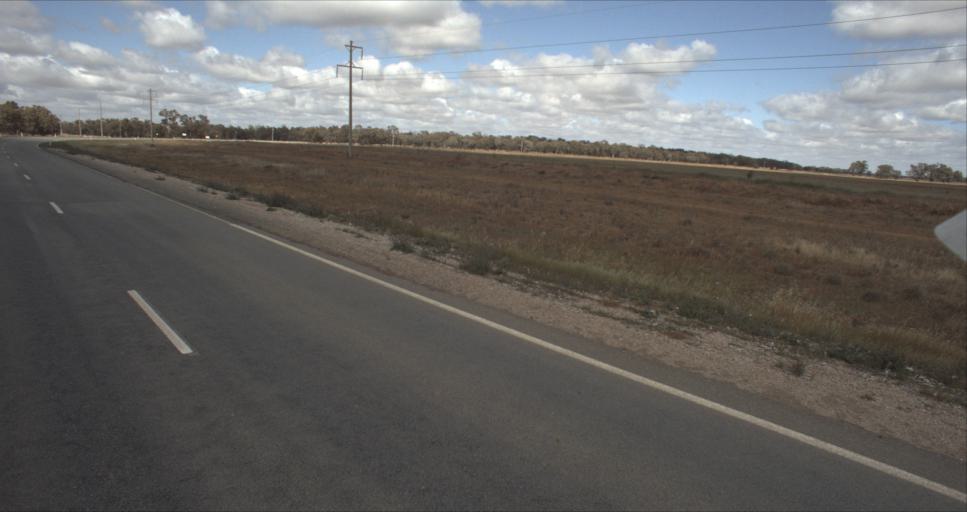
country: AU
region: New South Wales
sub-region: Murrumbidgee Shire
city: Darlington Point
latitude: -34.5939
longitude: 146.1631
